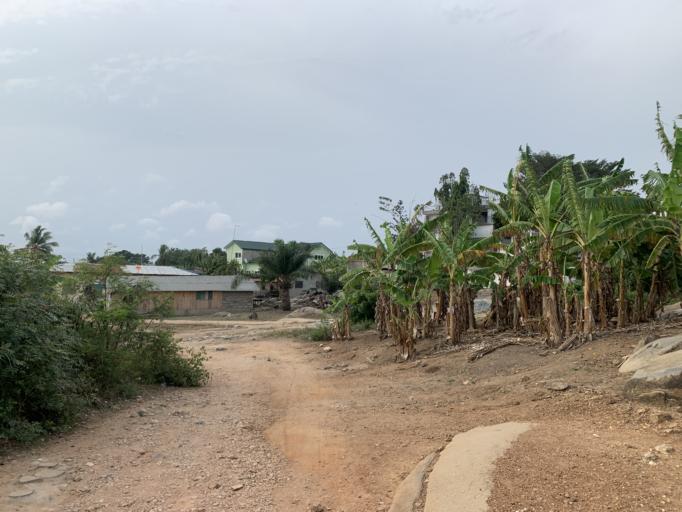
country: GH
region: Central
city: Winneba
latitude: 5.3594
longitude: -0.6285
